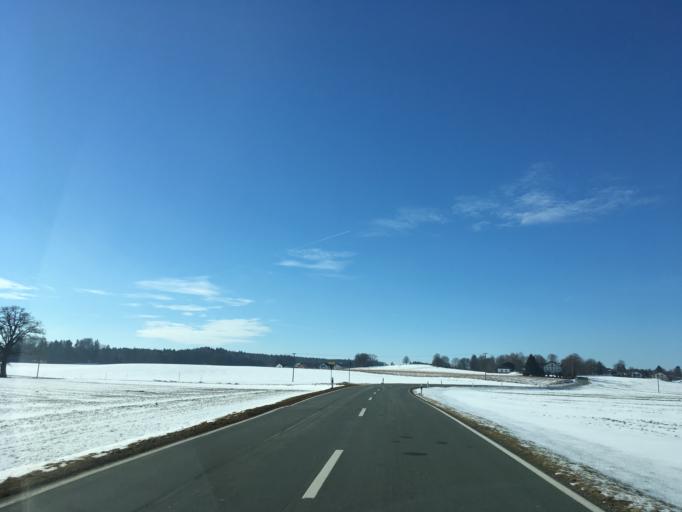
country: DE
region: Bavaria
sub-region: Upper Bavaria
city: Albaching
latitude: 48.1143
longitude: 12.1400
